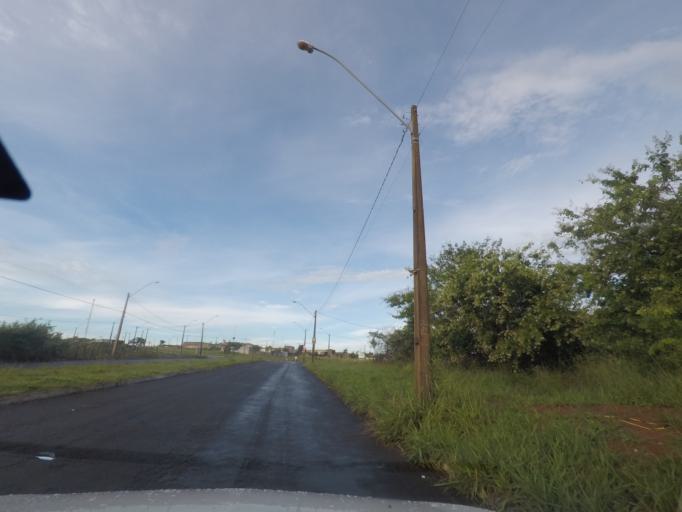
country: BR
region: Goias
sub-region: Goiania
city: Goiania
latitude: -16.7507
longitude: -49.3768
